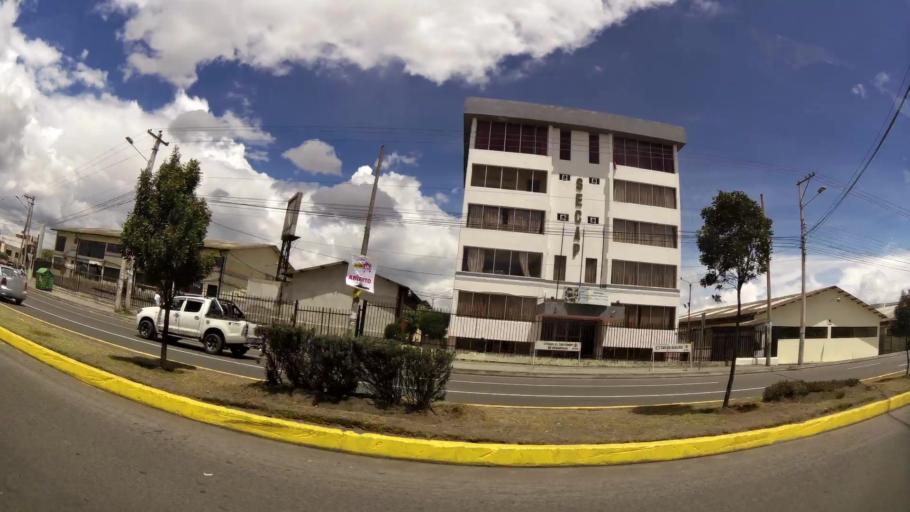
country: EC
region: Tungurahua
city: Ambato
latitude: -1.2685
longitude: -78.6117
